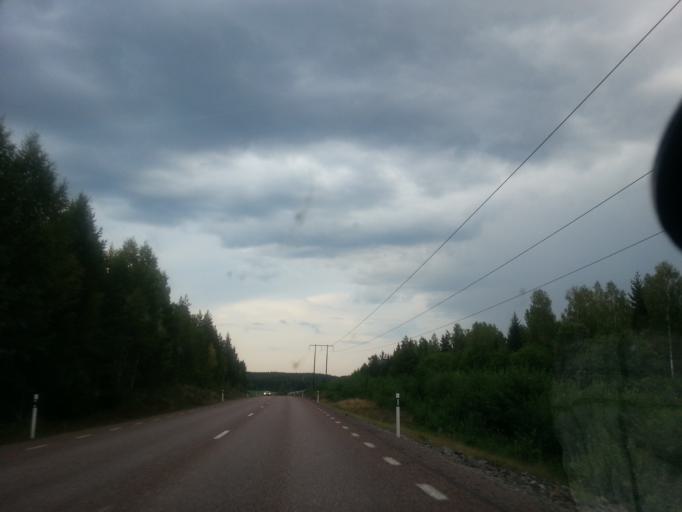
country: SE
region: Gaevleborg
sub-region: Hofors Kommun
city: Hofors
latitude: 60.5317
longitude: 16.4572
